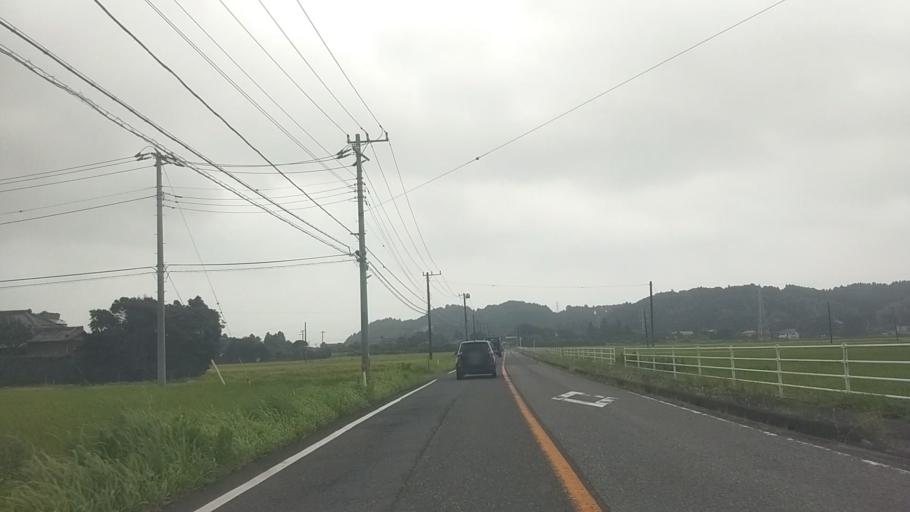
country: JP
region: Chiba
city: Ohara
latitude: 35.2632
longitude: 140.3730
